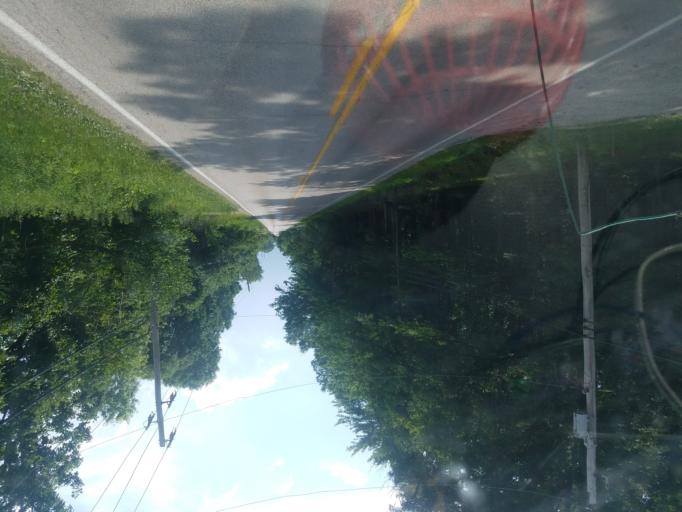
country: US
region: Ohio
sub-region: Portage County
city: Ravenna
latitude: 41.0985
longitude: -81.2089
